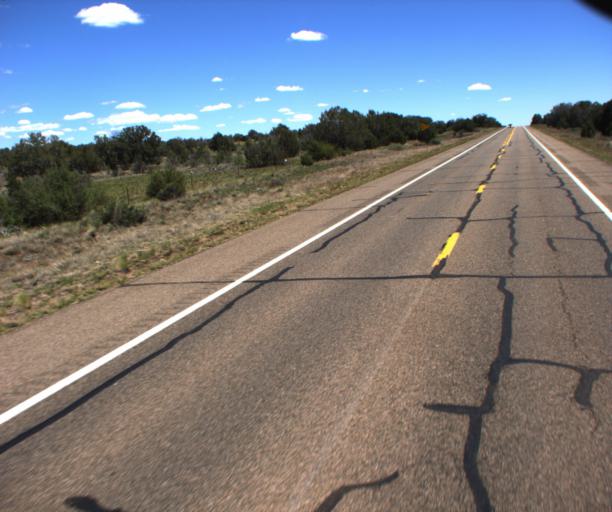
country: US
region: Arizona
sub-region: Coconino County
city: Williams
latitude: 35.1770
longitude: -112.4637
